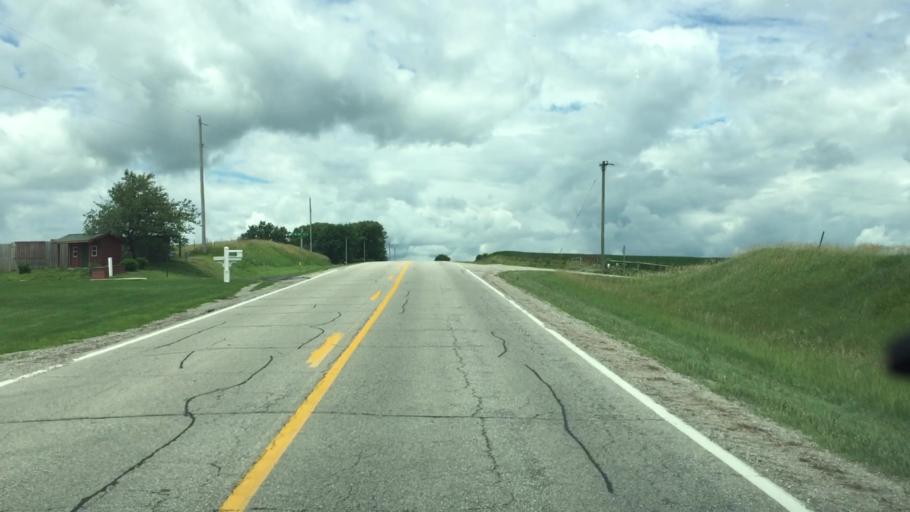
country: US
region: Iowa
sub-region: Jasper County
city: Monroe
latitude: 41.5736
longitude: -93.0821
